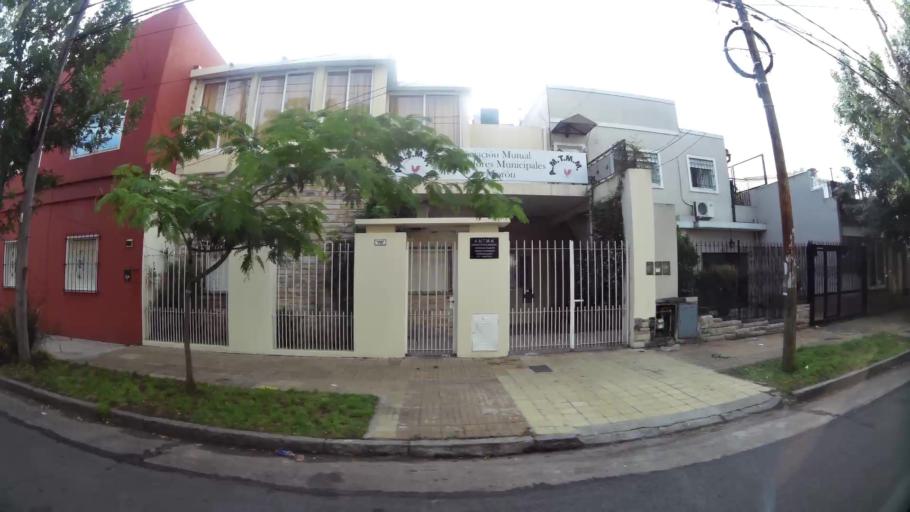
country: AR
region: Buenos Aires
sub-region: Partido de Moron
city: Moron
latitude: -34.6563
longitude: -58.6214
